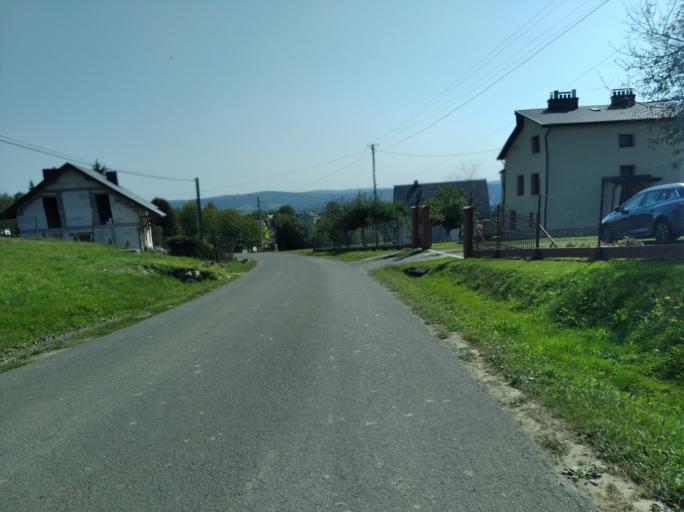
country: PL
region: Subcarpathian Voivodeship
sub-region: Powiat strzyzowski
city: Czudec
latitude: 49.9530
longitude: 21.8310
